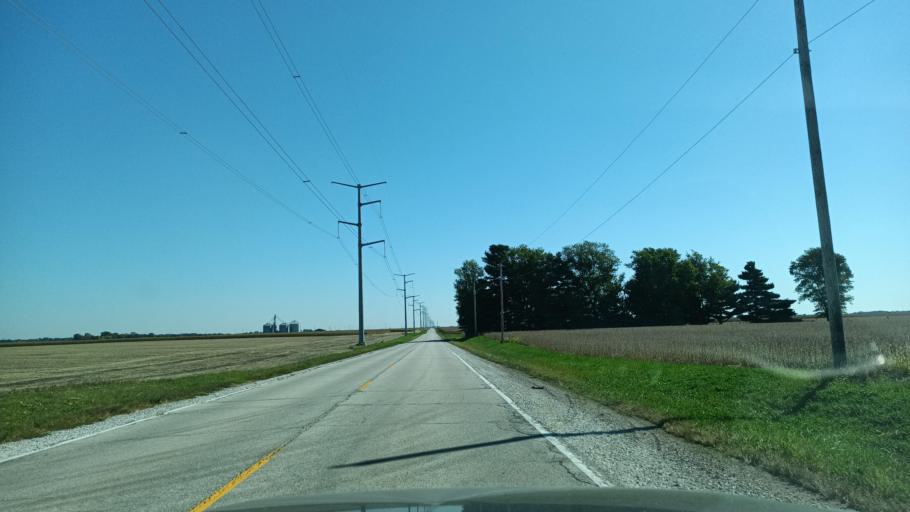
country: US
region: Illinois
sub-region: Peoria County
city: Elmwood
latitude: 40.9024
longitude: -90.0334
